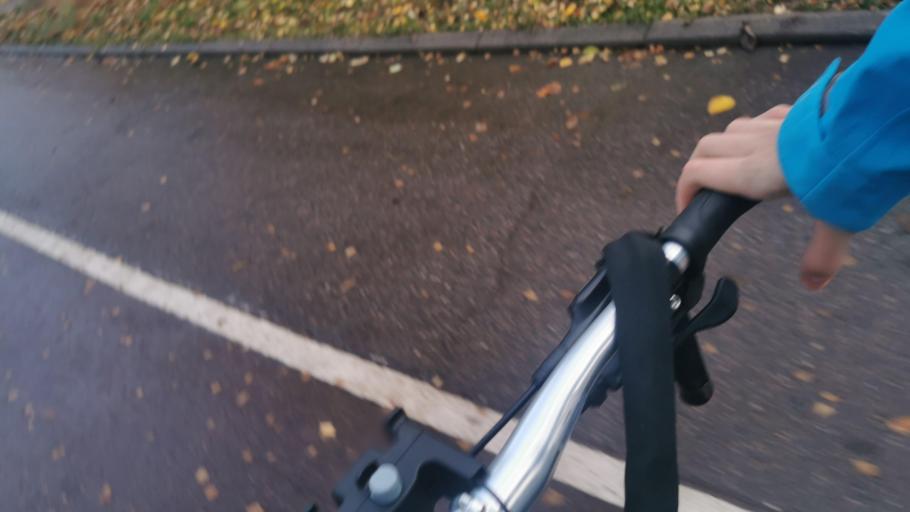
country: FI
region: Uusimaa
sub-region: Helsinki
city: Kerava
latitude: 60.4065
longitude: 25.0913
